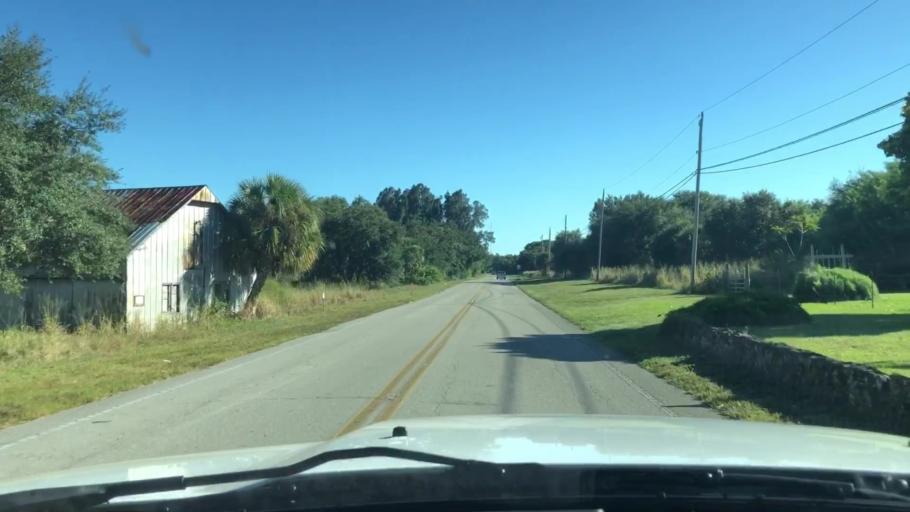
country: US
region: Florida
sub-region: Indian River County
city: Florida Ridge
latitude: 27.5711
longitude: -80.3746
